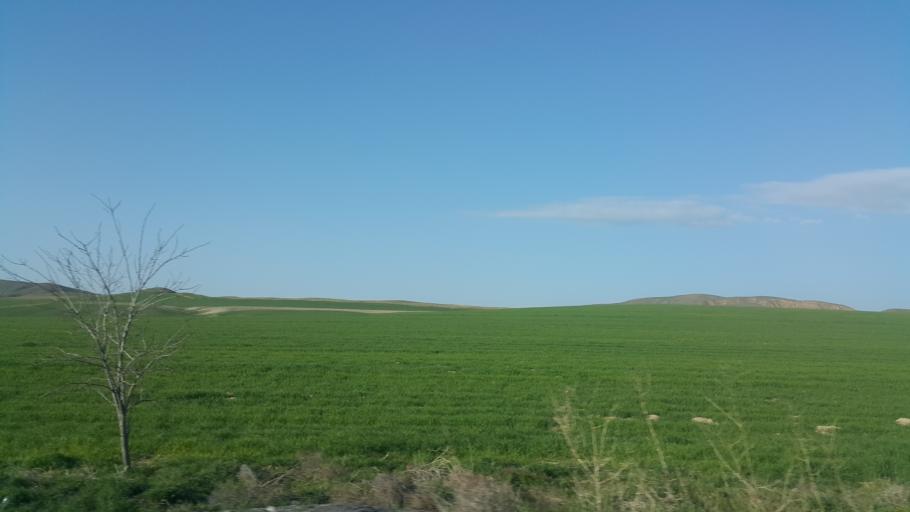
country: TR
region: Ankara
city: Sereflikochisar
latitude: 39.1131
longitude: 33.3625
